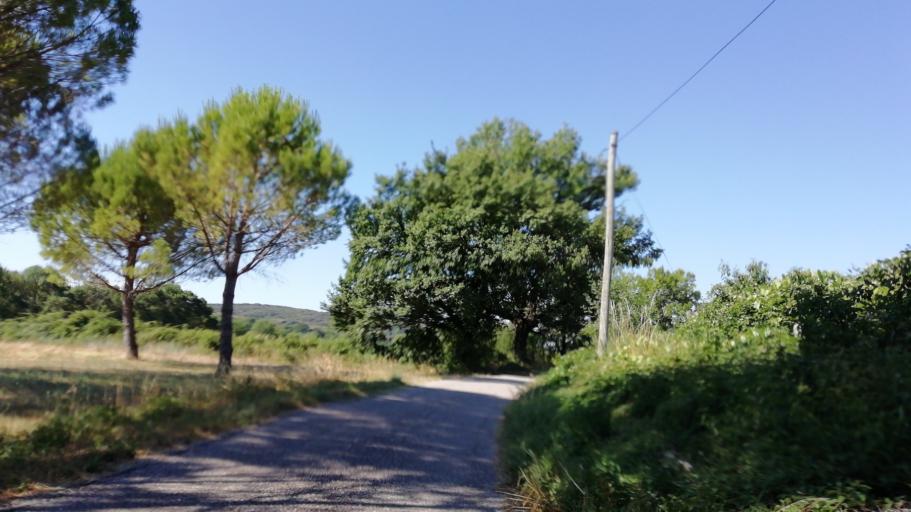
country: FR
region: Languedoc-Roussillon
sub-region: Departement de l'Herault
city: Saint-Martin-de-Londres
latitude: 43.7895
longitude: 3.7471
